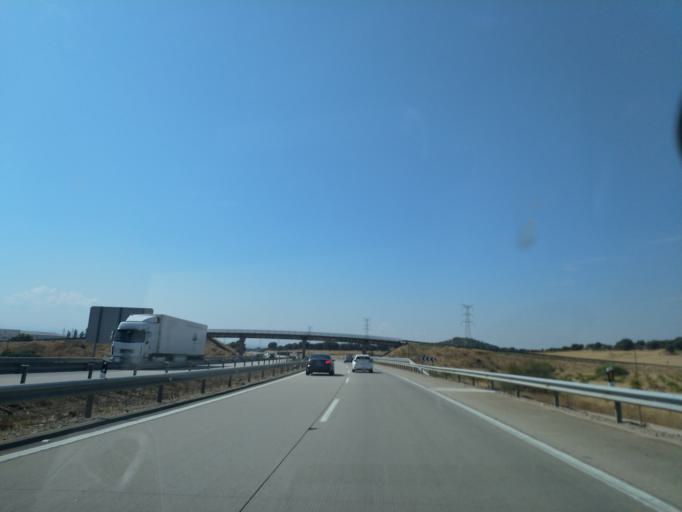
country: ES
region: Castille-La Mancha
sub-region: Province of Toledo
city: Talavera de la Reina
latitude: 40.0024
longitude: -4.8306
